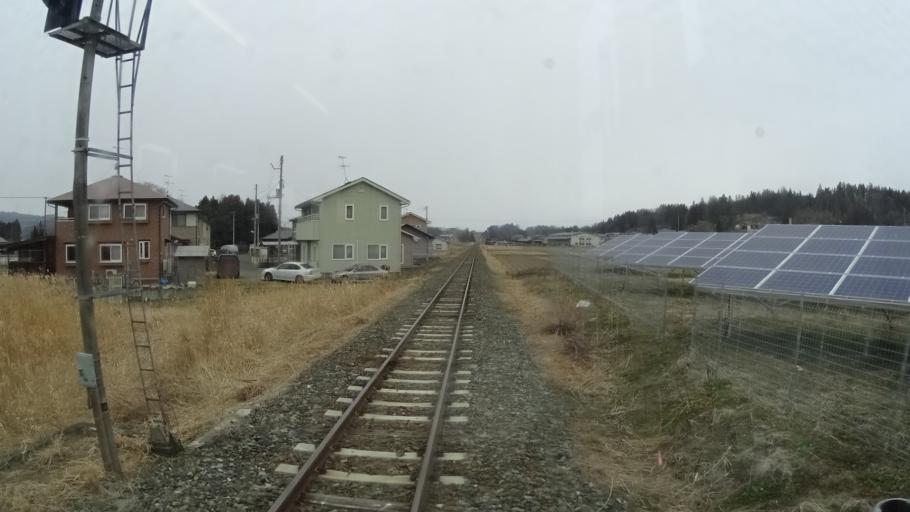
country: JP
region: Iwate
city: Hanamaki
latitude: 39.3796
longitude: 141.2385
